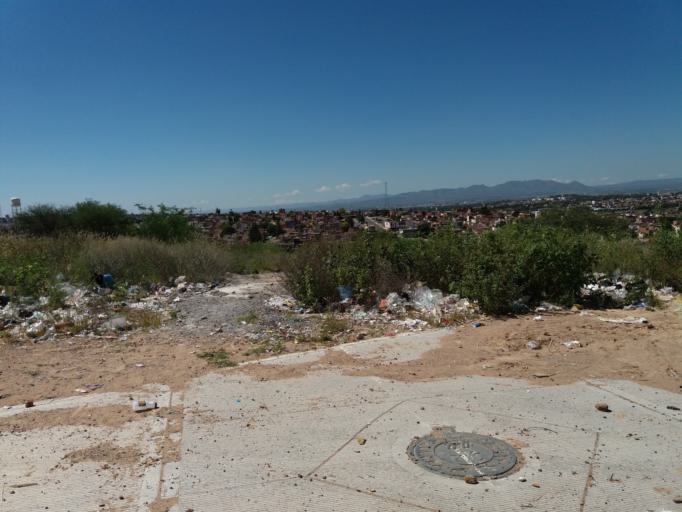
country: MX
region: Aguascalientes
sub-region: Aguascalientes
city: Cumbres III
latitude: 21.8724
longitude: -102.2299
